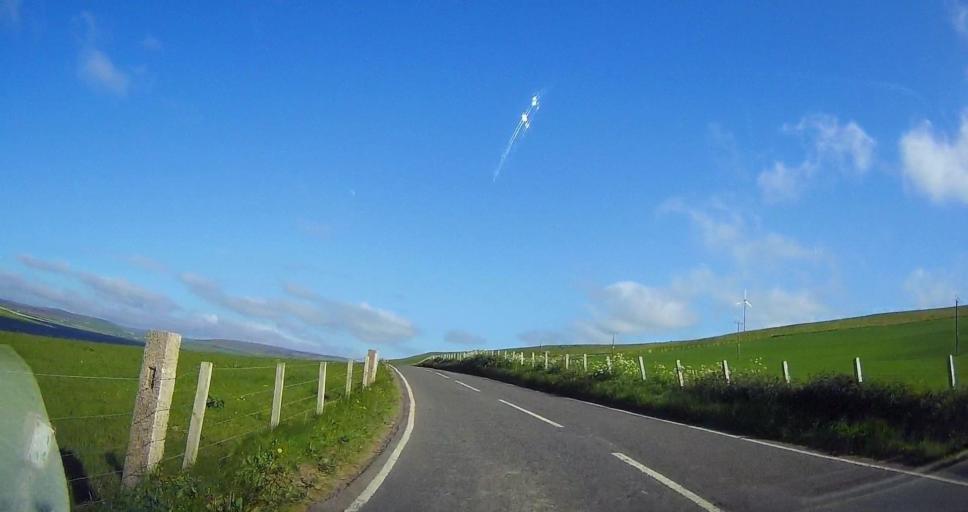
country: GB
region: Scotland
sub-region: Orkney Islands
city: Stromness
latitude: 59.1176
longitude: -3.3058
